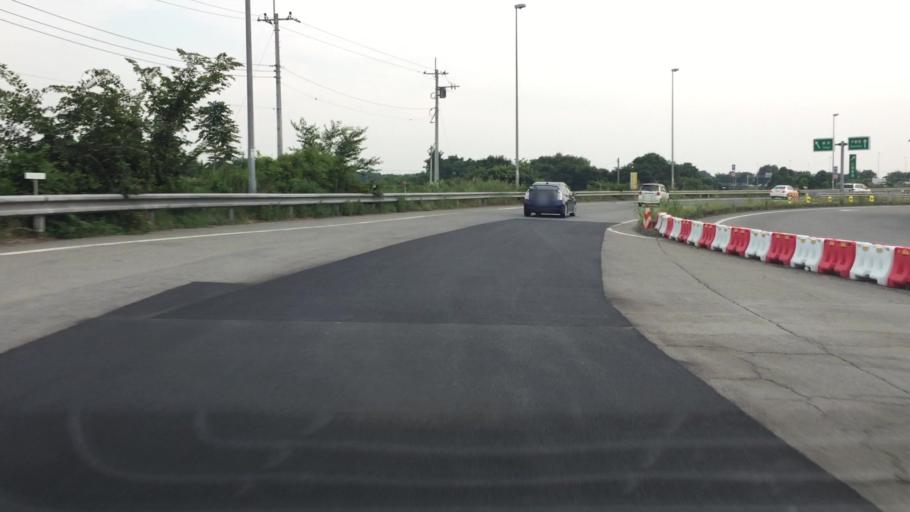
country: JP
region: Gunma
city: Tatebayashi
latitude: 36.2260
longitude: 139.5734
